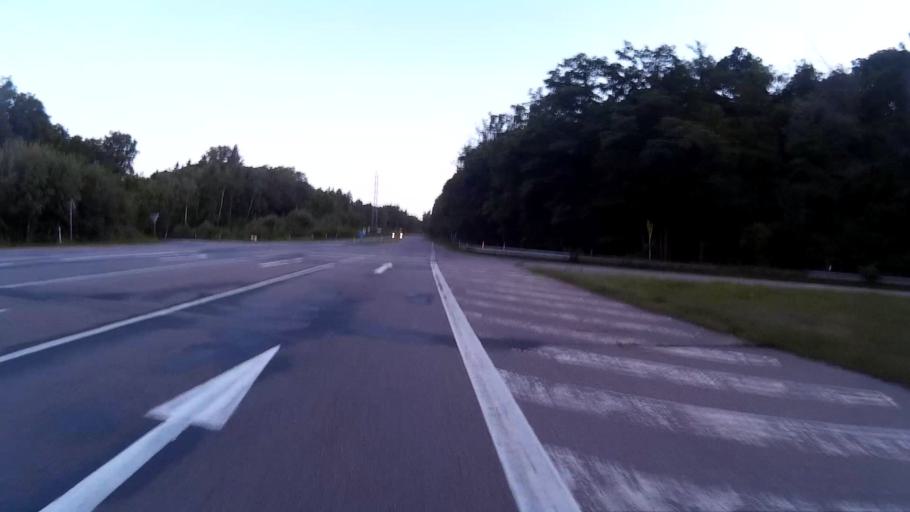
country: CZ
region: South Moravian
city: Troubsko
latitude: 49.2011
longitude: 16.5166
